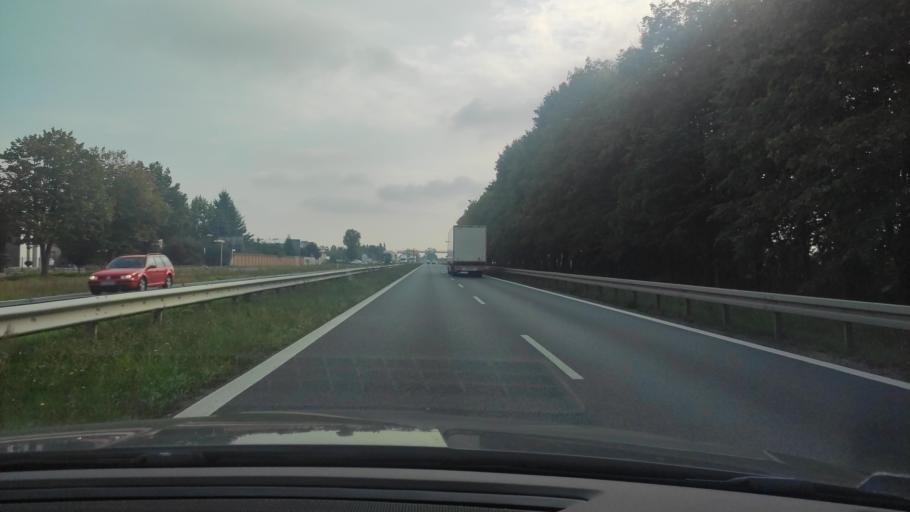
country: PL
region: Greater Poland Voivodeship
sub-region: Powiat poznanski
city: Swarzedz
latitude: 52.4002
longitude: 17.1457
